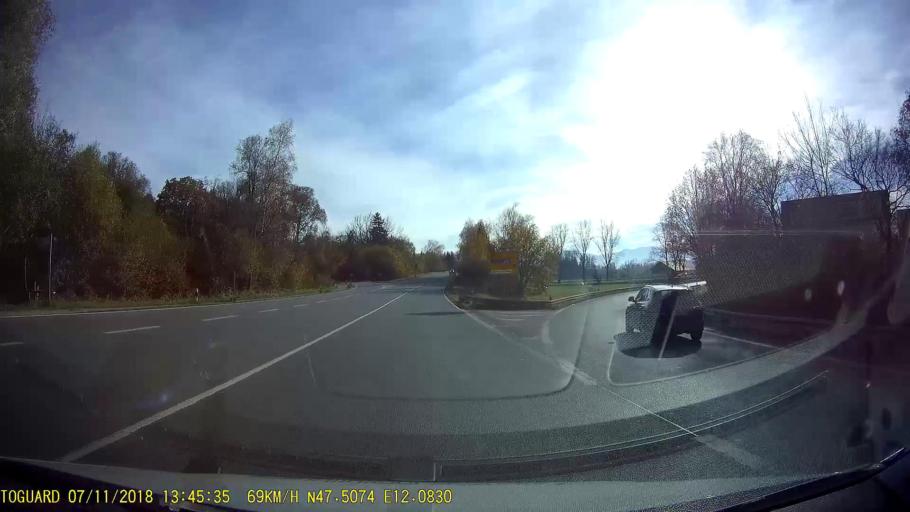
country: DE
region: Bavaria
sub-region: Upper Bavaria
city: Rosenheim
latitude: 47.8431
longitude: 12.1386
